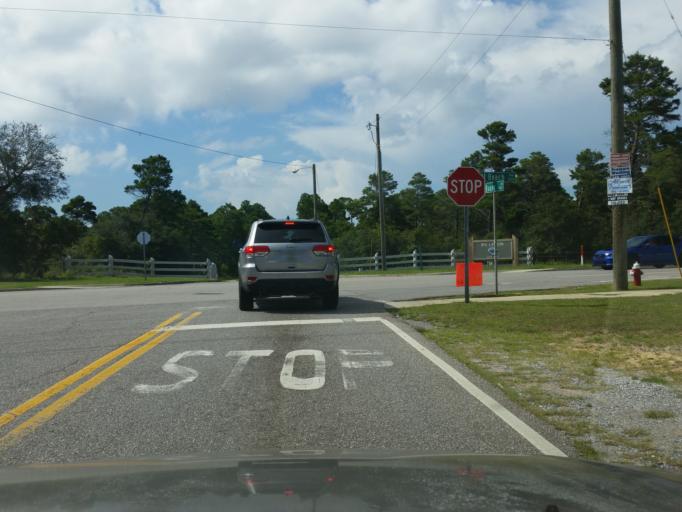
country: US
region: Florida
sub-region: Escambia County
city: Myrtle Grove
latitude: 30.3221
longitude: -87.4038
